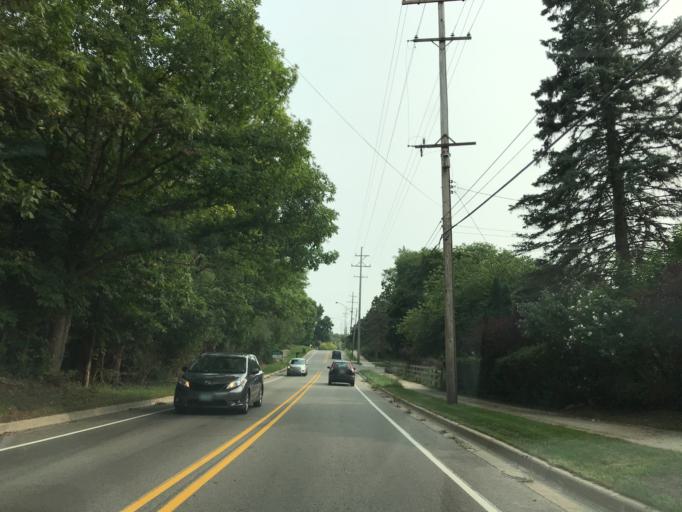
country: US
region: Michigan
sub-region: Ingham County
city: Okemos
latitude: 42.7286
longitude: -84.4474
